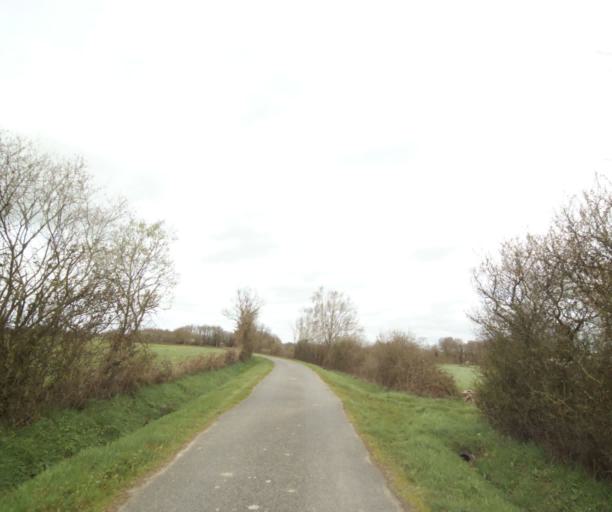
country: FR
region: Pays de la Loire
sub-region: Departement de la Loire-Atlantique
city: Bouvron
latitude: 47.4264
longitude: -1.8607
